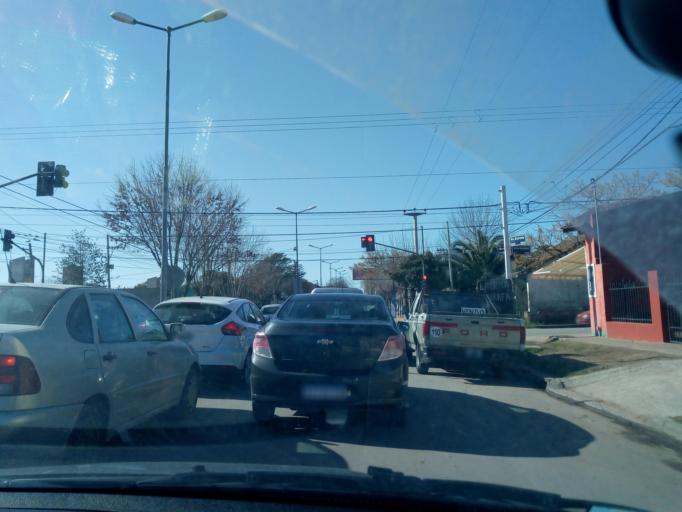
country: AR
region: Buenos Aires
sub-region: Partido de Tandil
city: Tandil
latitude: -37.3392
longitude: -59.1470
